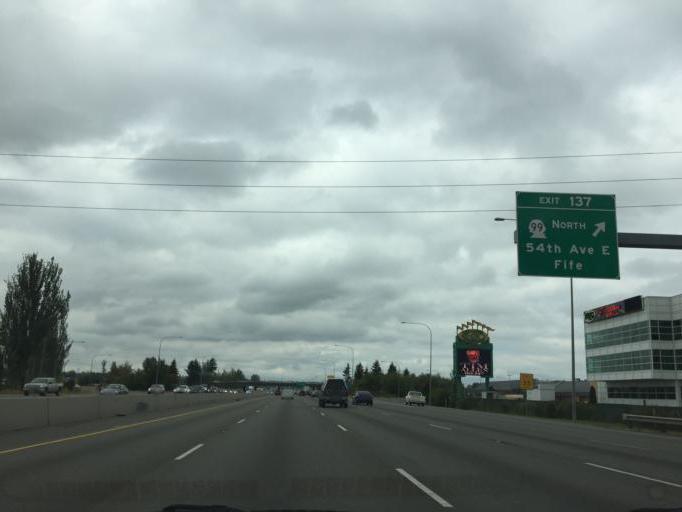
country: US
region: Washington
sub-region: Pierce County
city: Fife
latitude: 47.2411
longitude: -122.3511
